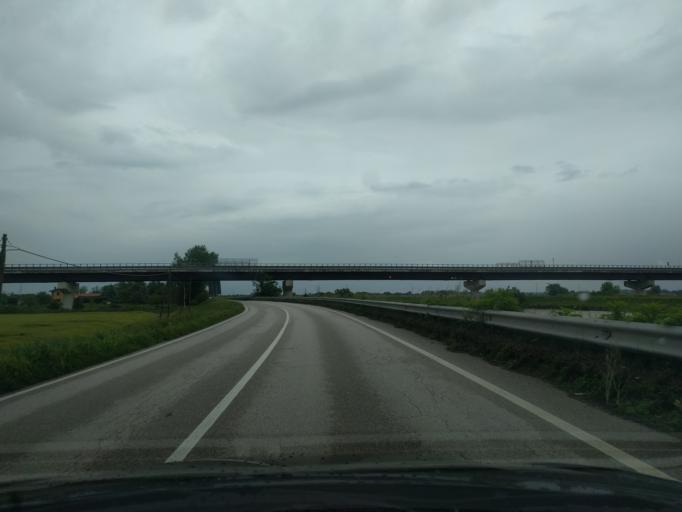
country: IT
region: Veneto
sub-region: Provincia di Rovigo
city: Bottrighe
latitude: 45.0471
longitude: 12.0994
